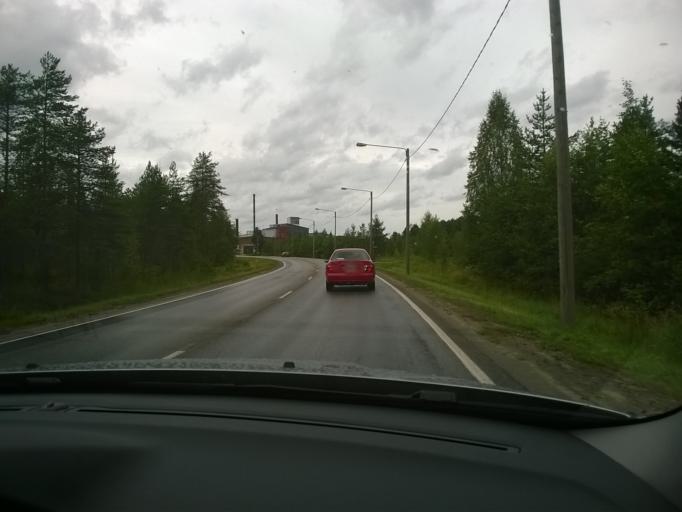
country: FI
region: Kainuu
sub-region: Kehys-Kainuu
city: Kuhmo
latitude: 64.1297
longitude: 29.4999
